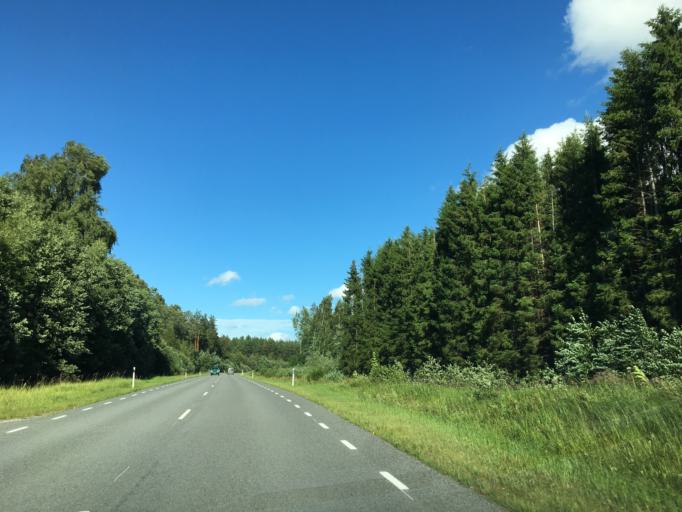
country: EE
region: Paernumaa
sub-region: Vaendra vald (alev)
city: Vandra
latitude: 58.5775
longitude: 25.2232
